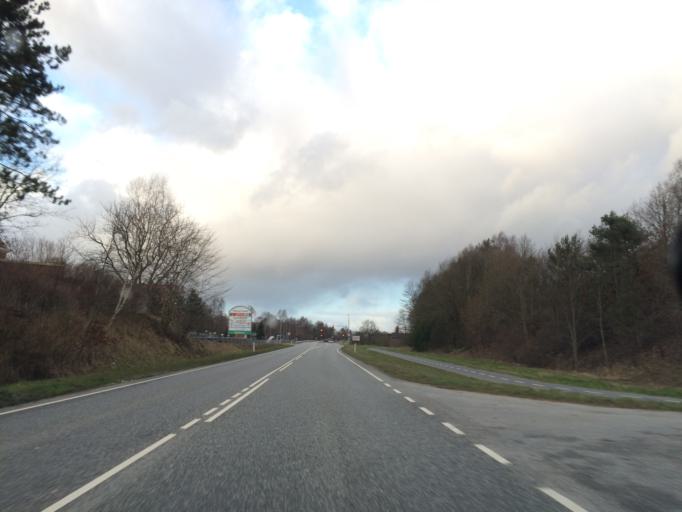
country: DK
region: Central Jutland
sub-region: Silkeborg Kommune
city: Virklund
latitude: 56.1298
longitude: 9.5634
